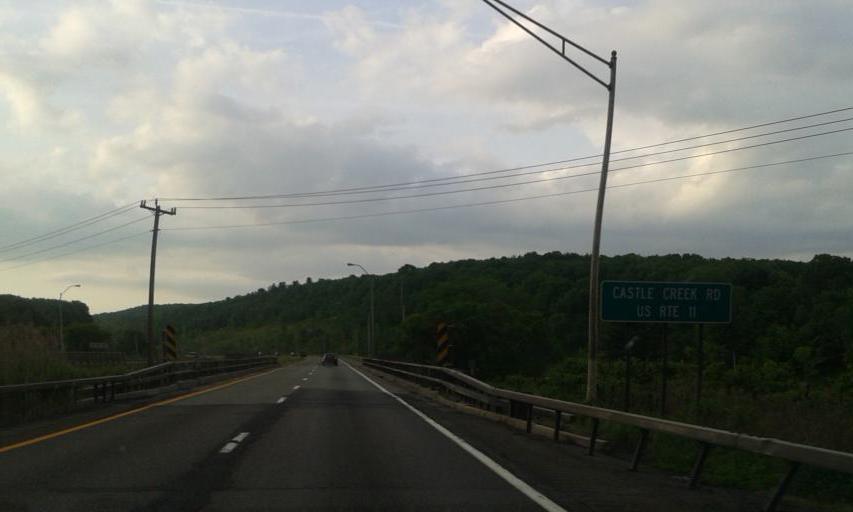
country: US
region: New York
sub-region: Broome County
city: Port Dickinson
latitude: 42.1636
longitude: -75.8962
